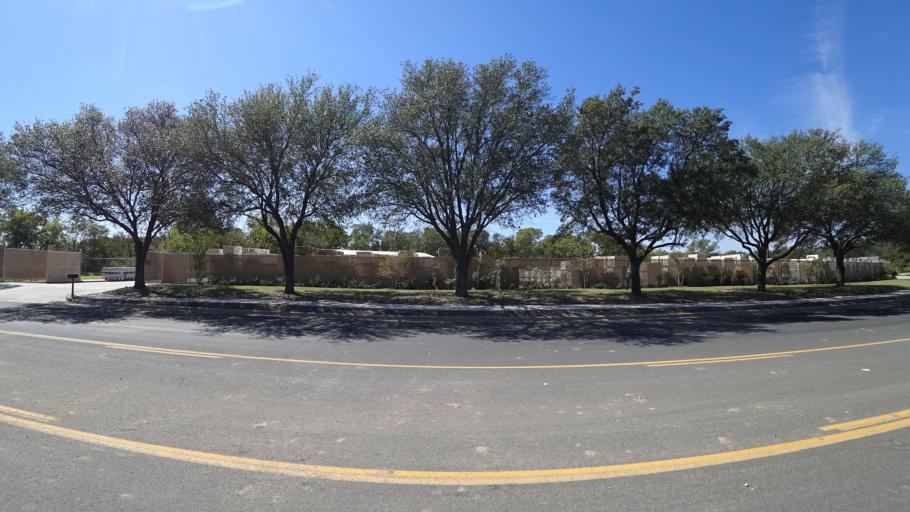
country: US
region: Texas
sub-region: Travis County
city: Austin
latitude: 30.2740
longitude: -97.6694
